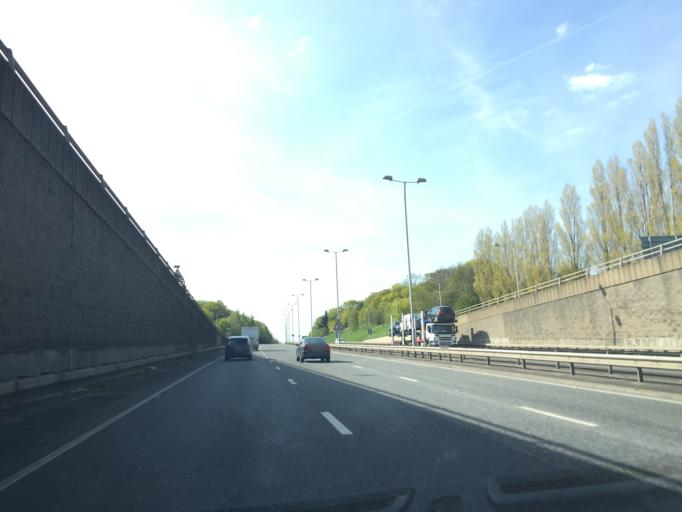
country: GB
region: England
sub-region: Greater London
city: Sidcup
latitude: 51.4191
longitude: 0.0970
